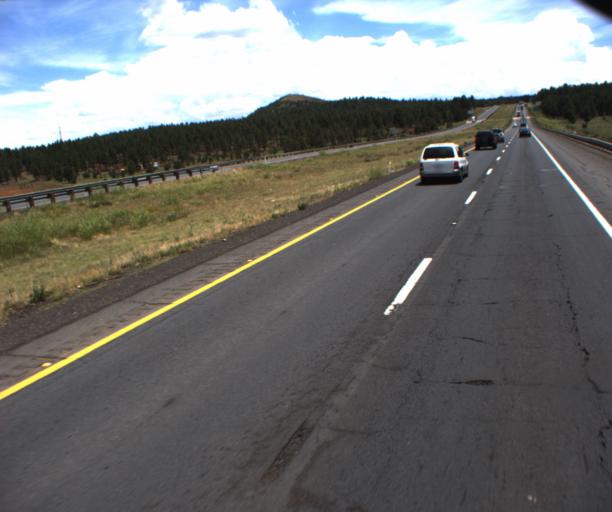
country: US
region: Arizona
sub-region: Coconino County
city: Williams
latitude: 35.2638
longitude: -112.1784
